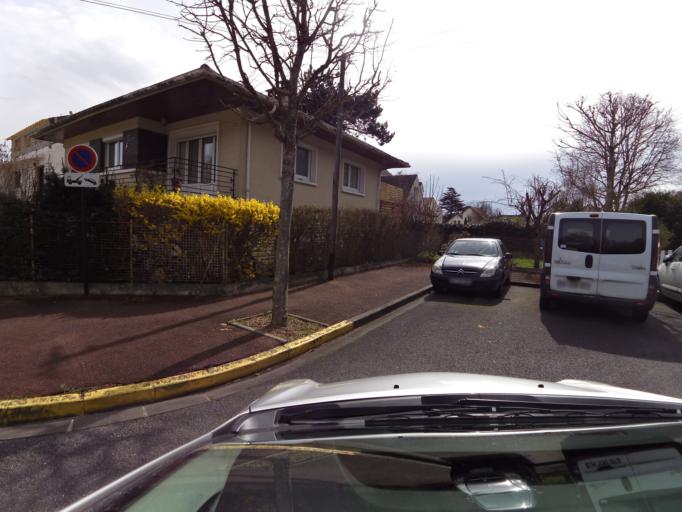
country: FR
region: Ile-de-France
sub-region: Departement de Seine-Saint-Denis
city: Tremblay-en-France
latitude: 48.9424
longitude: 2.5669
